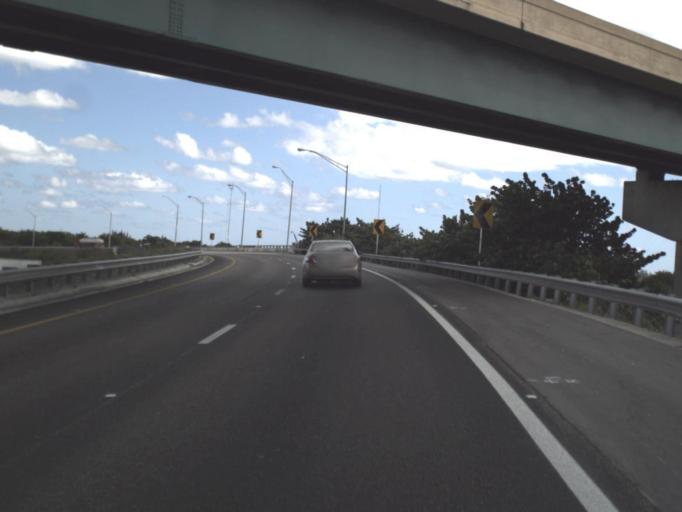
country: US
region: Florida
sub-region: Miami-Dade County
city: Lake Lucerne
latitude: 25.9728
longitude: -80.2313
